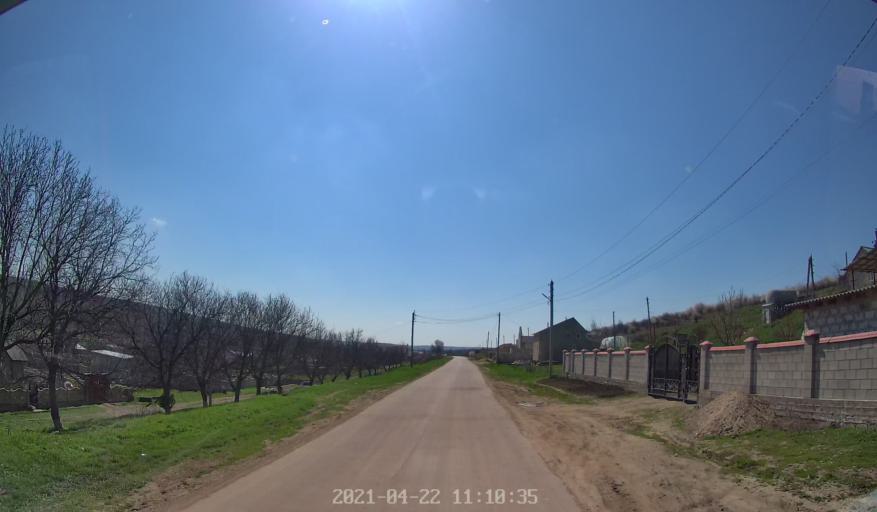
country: MD
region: Chisinau
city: Ciorescu
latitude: 47.1609
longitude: 28.9535
